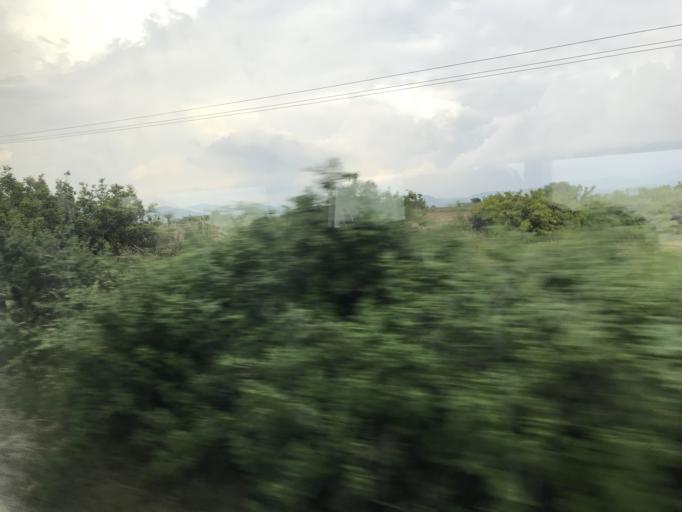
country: GR
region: East Macedonia and Thrace
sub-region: Nomos Rodopis
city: Sapes
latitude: 40.9761
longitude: 25.6460
